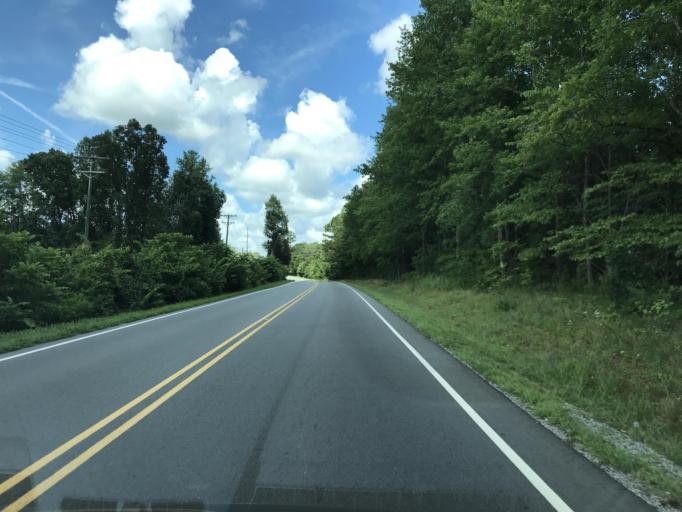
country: US
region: North Carolina
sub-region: Lincoln County
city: Pumpkin Center
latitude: 35.5112
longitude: -81.1571
